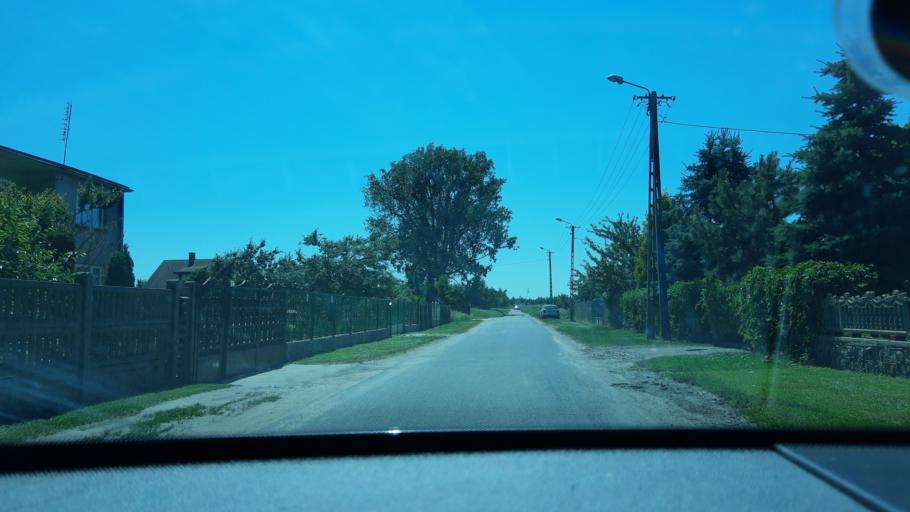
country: PL
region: Lodz Voivodeship
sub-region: Powiat sieradzki
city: Sieradz
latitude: 51.5726
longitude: 18.7434
